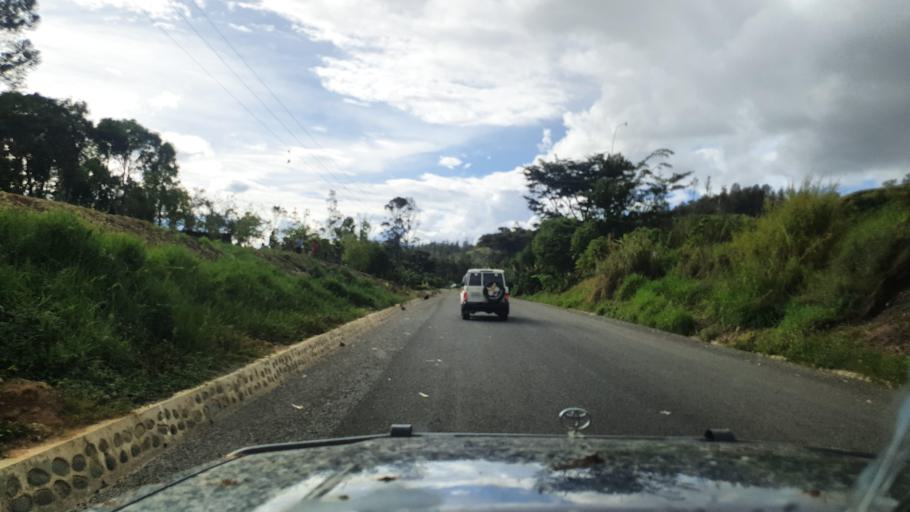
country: PG
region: Jiwaka
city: Minj
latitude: -5.9068
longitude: 144.7532
